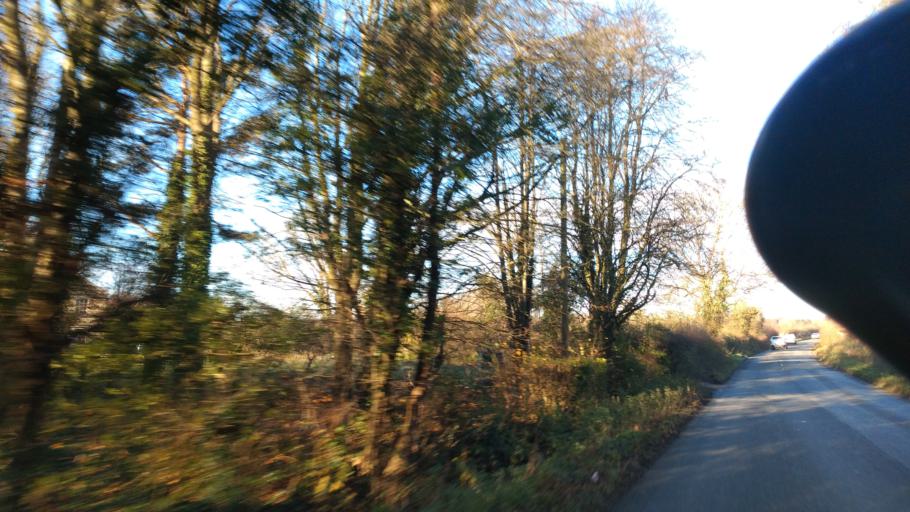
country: GB
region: England
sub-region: Wiltshire
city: Wingfield
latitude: 51.3171
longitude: -2.2579
